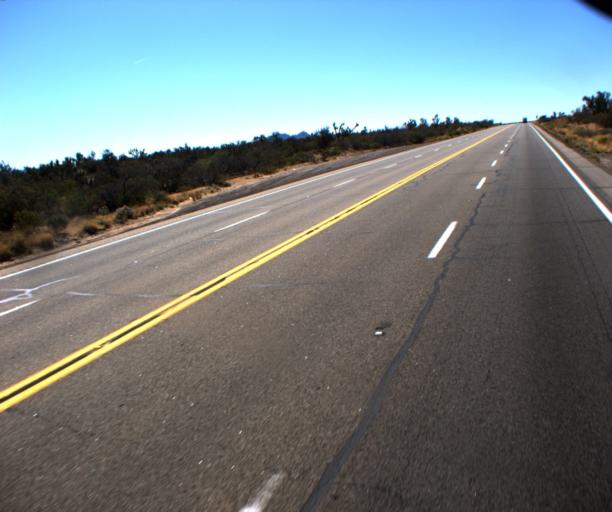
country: US
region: Arizona
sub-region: Yavapai County
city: Congress
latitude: 34.2810
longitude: -113.1028
